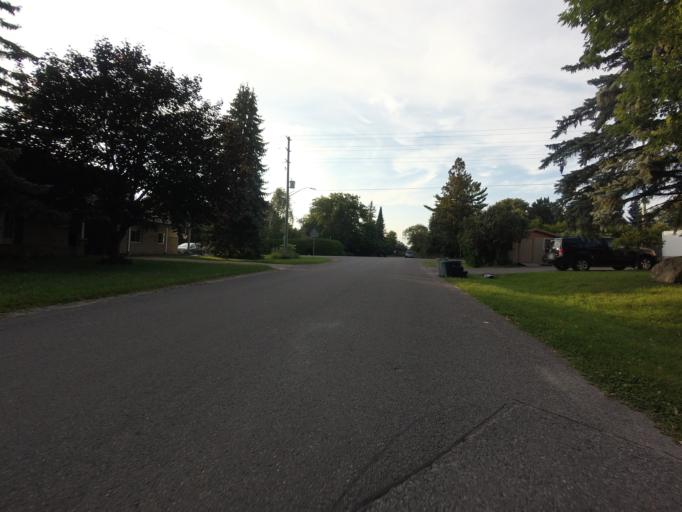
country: CA
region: Ontario
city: Ottawa
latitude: 45.3446
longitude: -75.7412
